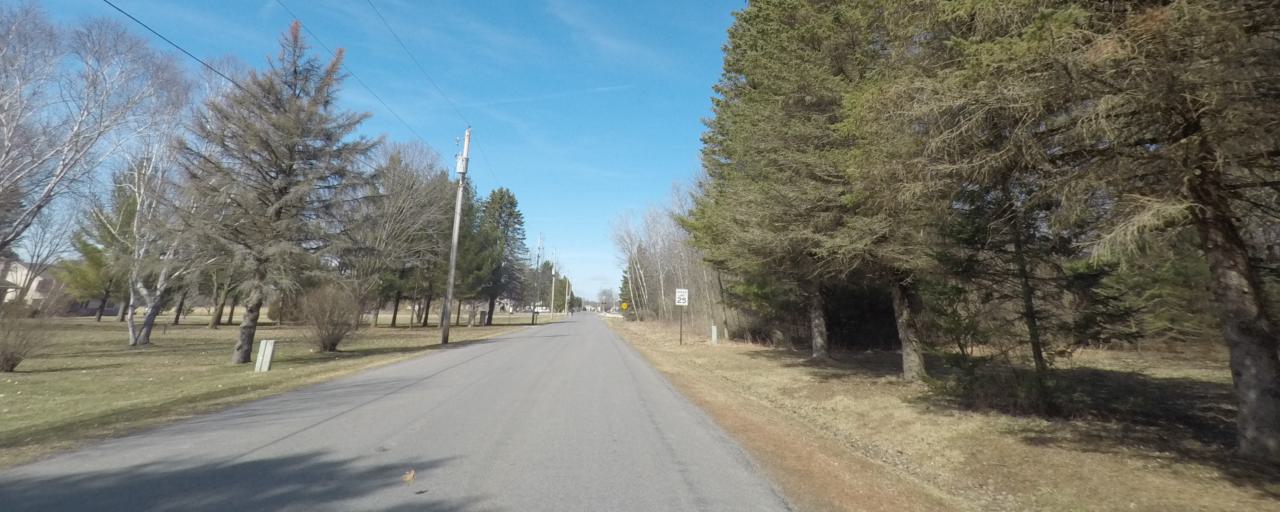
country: US
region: Wisconsin
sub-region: Waukesha County
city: Merton
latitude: 43.1578
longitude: -88.3215
